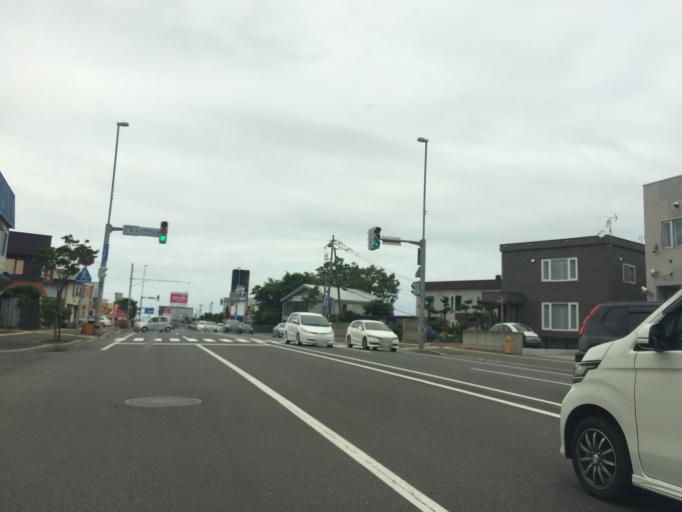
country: JP
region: Hokkaido
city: Sapporo
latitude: 43.1194
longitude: 141.2383
